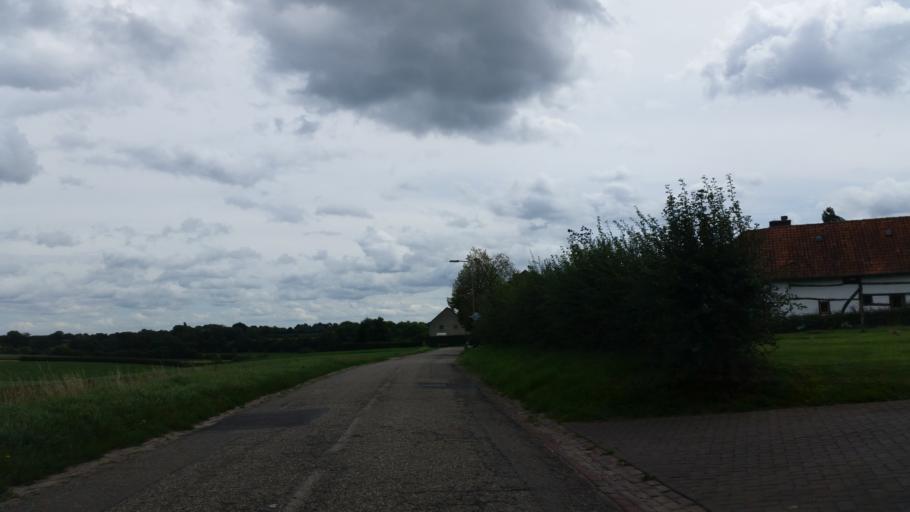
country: NL
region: Limburg
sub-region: Eijsden-Margraten
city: Margraten
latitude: 50.8319
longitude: 5.7953
